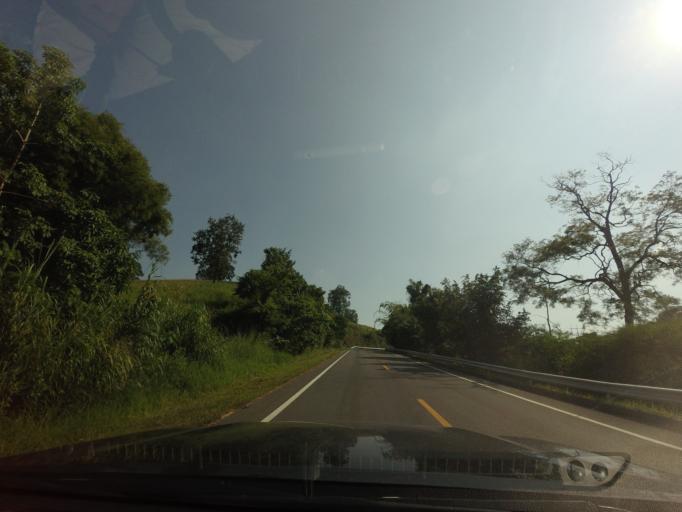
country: TH
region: Nan
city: Santi Suk
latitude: 18.9228
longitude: 100.8936
